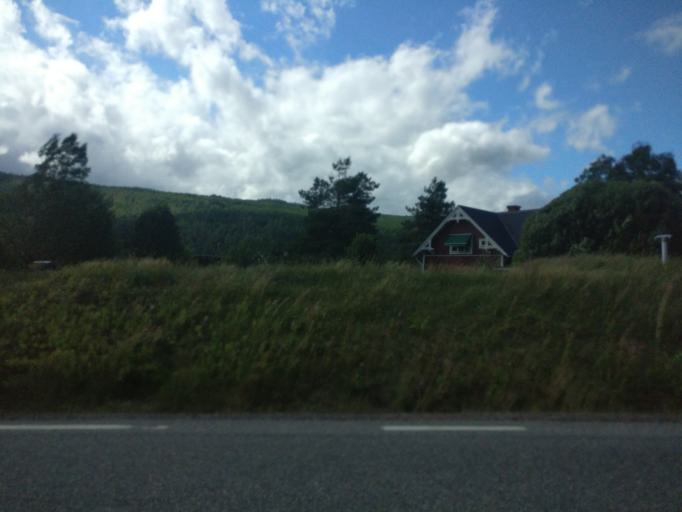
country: SE
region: Vaermland
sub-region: Hagfors Kommun
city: Ekshaerad
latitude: 60.2937
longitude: 13.3930
